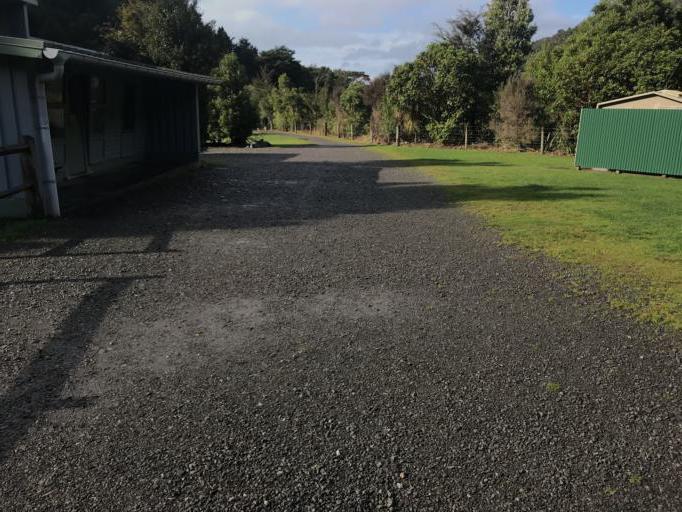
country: NZ
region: Wellington
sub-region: Masterton District
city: Masterton
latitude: -40.9065
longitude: 175.4764
